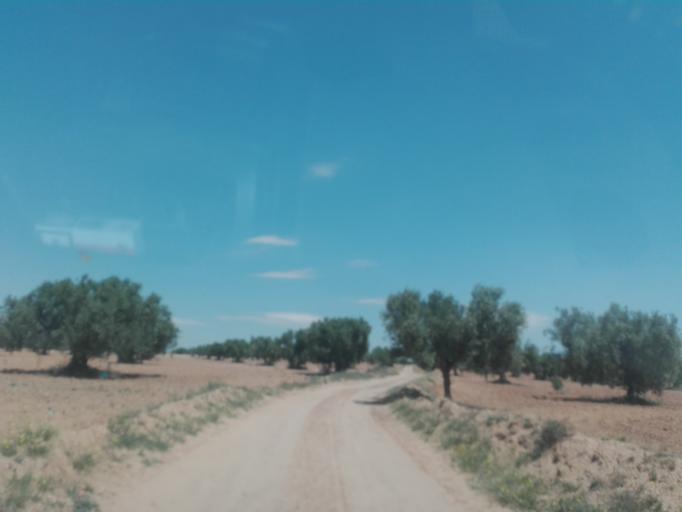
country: TN
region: Safaqis
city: Sfax
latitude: 34.6714
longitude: 10.6077
